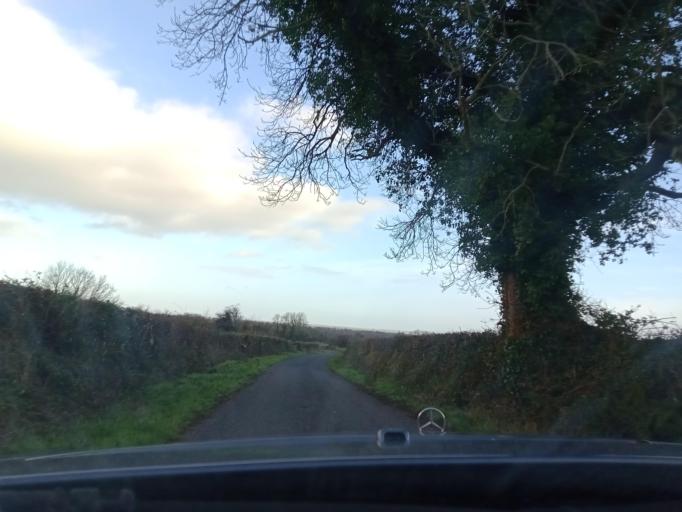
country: IE
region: Leinster
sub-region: Kilkenny
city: Callan
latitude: 52.4683
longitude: -7.3935
